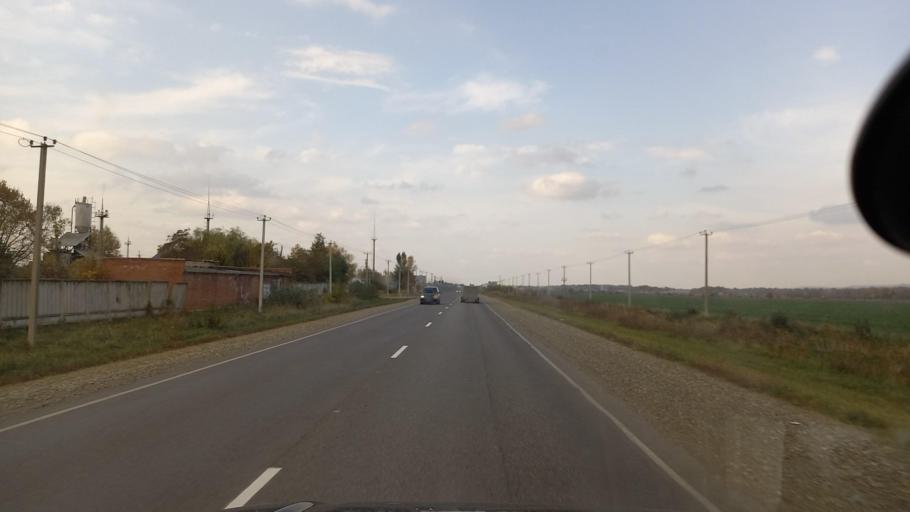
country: RU
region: Krasnodarskiy
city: Mostovskoy
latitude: 44.3793
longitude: 40.8224
